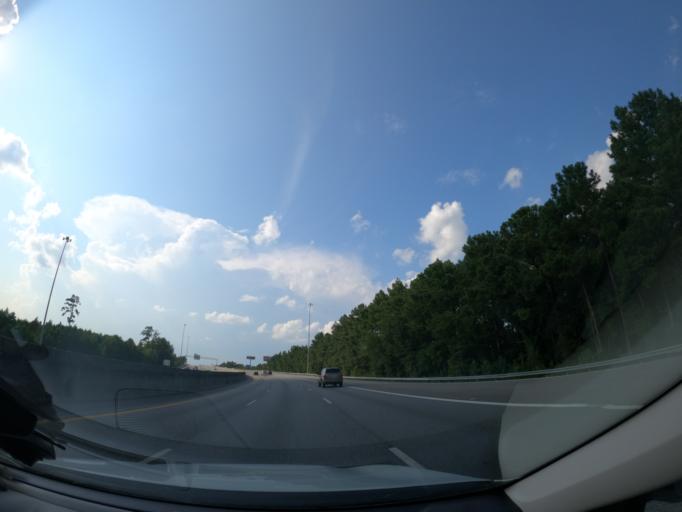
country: US
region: Georgia
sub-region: Columbia County
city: Martinez
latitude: 33.4534
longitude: -82.0740
